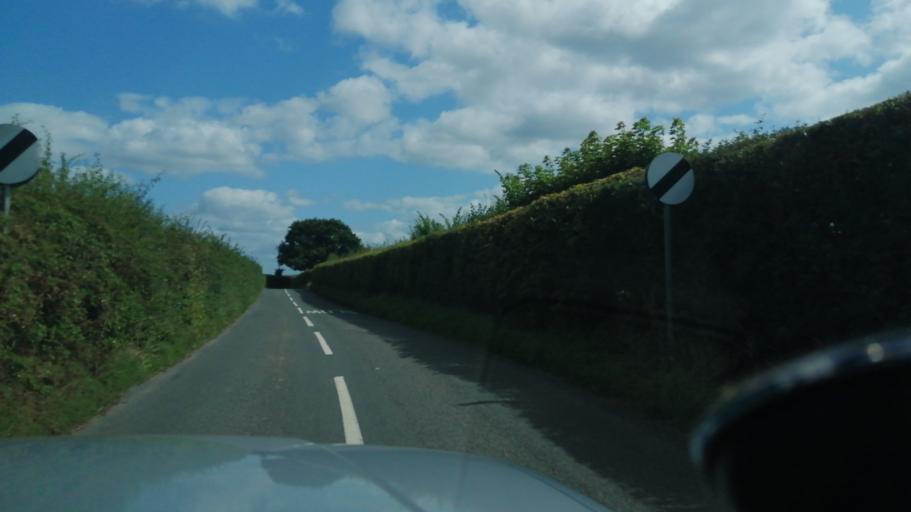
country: GB
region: England
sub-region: Herefordshire
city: Blakemere
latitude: 52.0592
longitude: -2.9281
